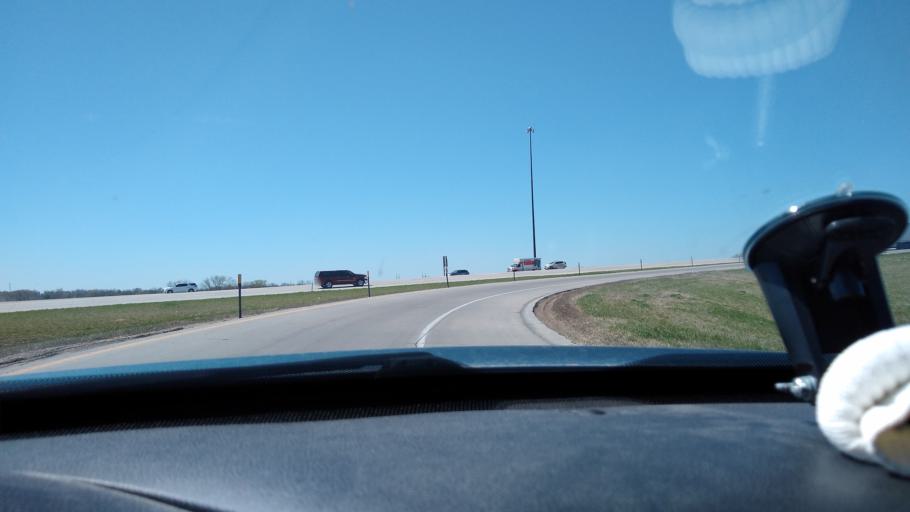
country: US
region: Nebraska
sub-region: Lancaster County
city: Waverly
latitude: 40.8953
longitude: -96.5637
